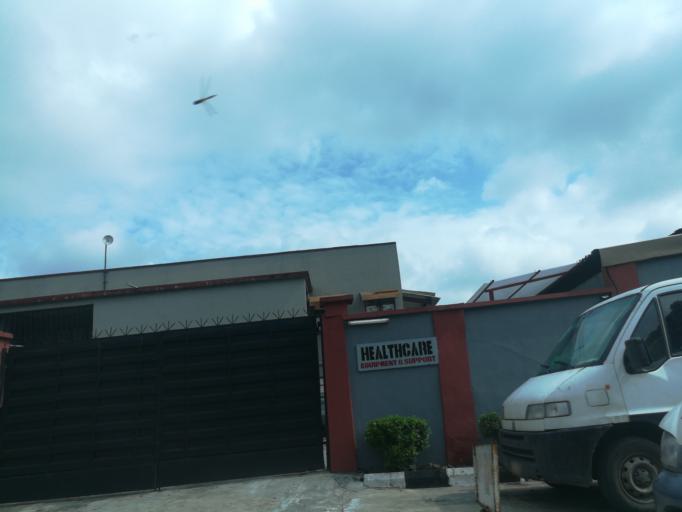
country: NG
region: Lagos
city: Somolu
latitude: 6.5595
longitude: 3.3627
